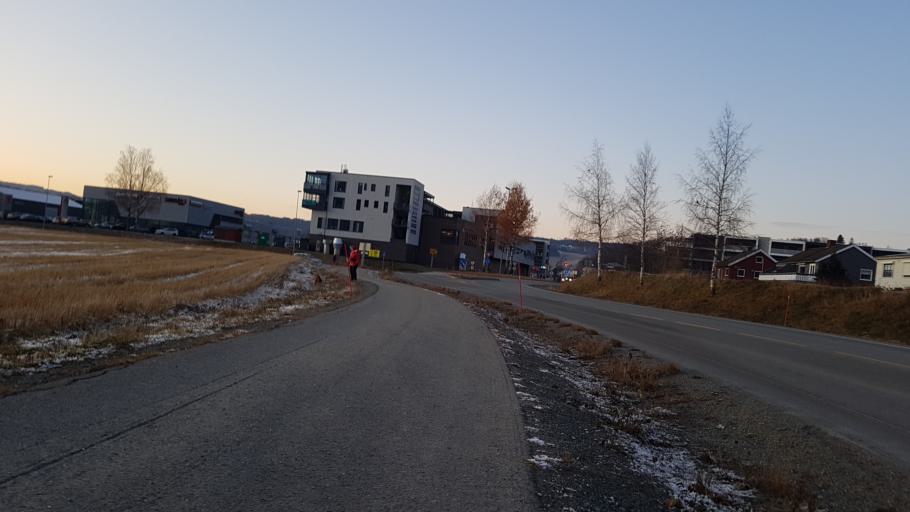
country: NO
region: Sor-Trondelag
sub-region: Melhus
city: Melhus
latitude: 63.2826
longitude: 10.2832
